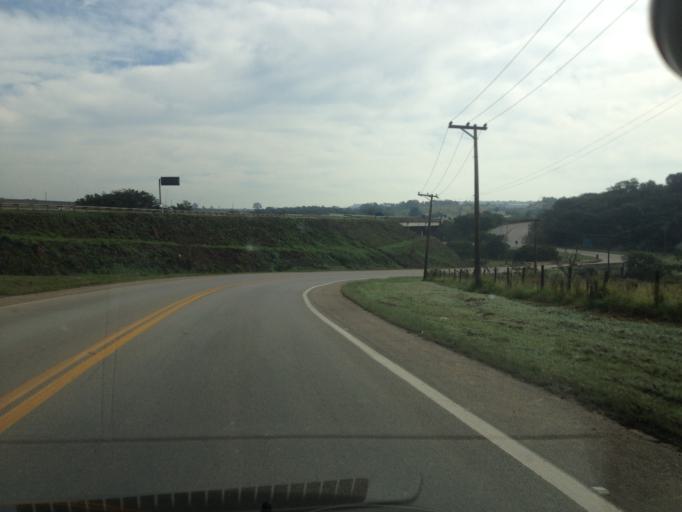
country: BR
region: Sao Paulo
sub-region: Itu
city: Itu
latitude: -23.2740
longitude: -47.3258
